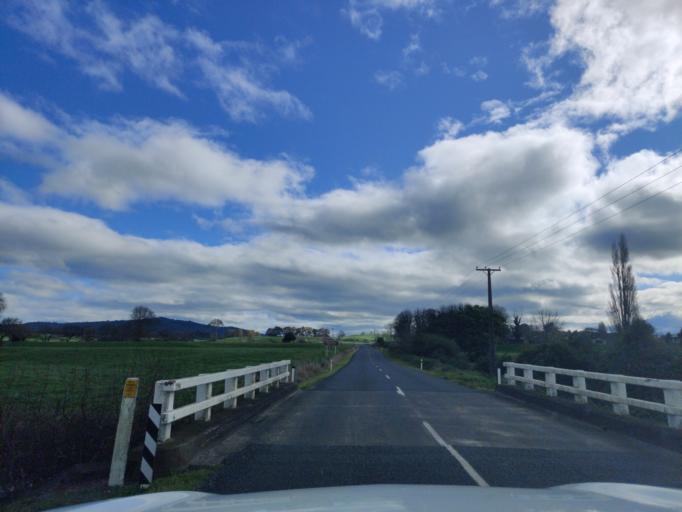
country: NZ
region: Waikato
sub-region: Matamata-Piako District
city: Matamata
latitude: -37.8762
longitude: 175.7268
